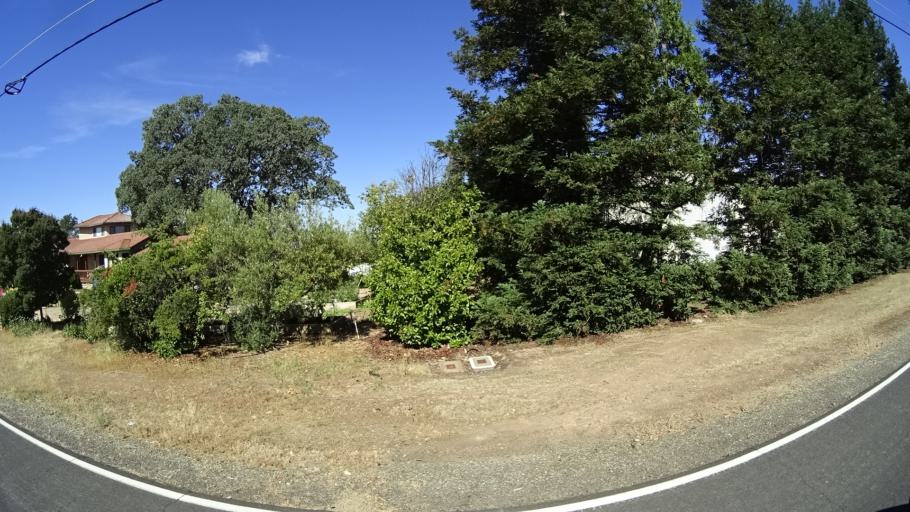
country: US
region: California
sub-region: Calaveras County
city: Valley Springs
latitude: 38.1719
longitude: -120.8618
